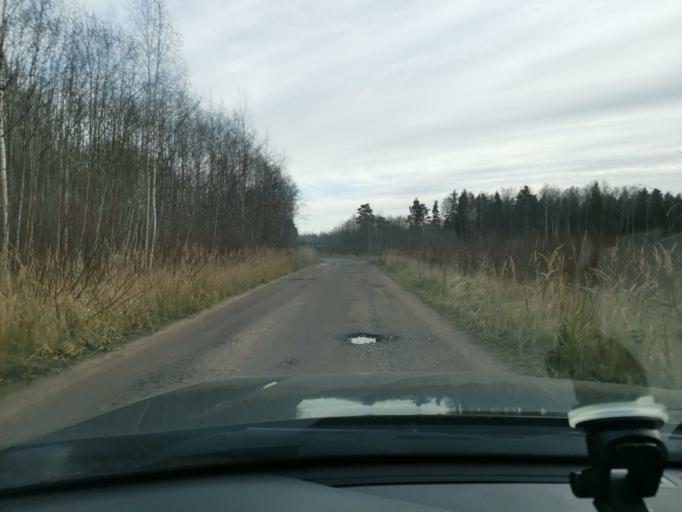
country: EE
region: Ida-Virumaa
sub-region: Sillamaee linn
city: Sillamae
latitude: 59.2589
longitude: 27.9126
